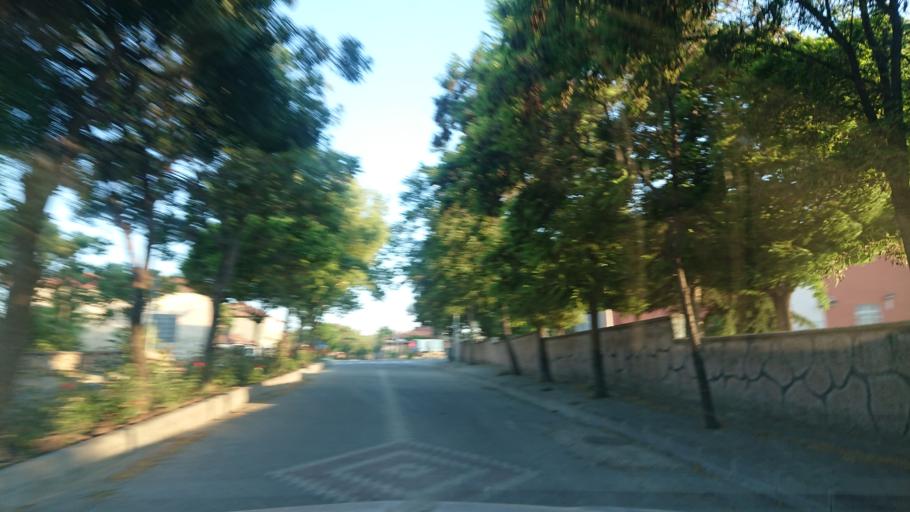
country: TR
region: Aksaray
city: Sariyahsi
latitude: 38.9864
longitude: 33.8444
